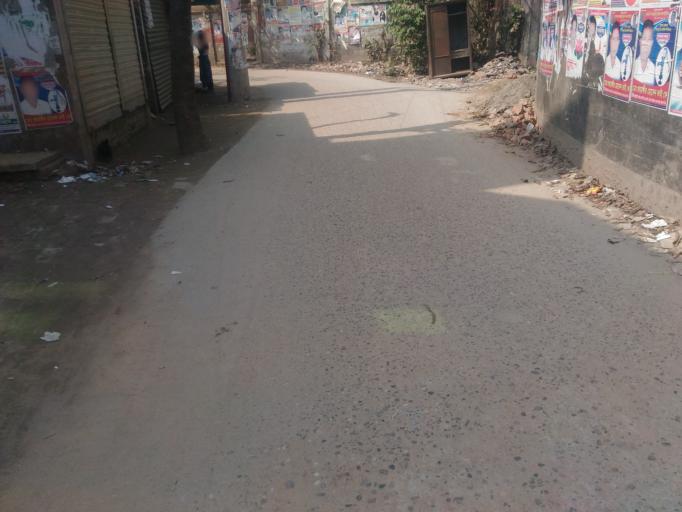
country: BD
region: Dhaka
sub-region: Dhaka
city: Dhaka
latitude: 23.6570
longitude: 90.4502
